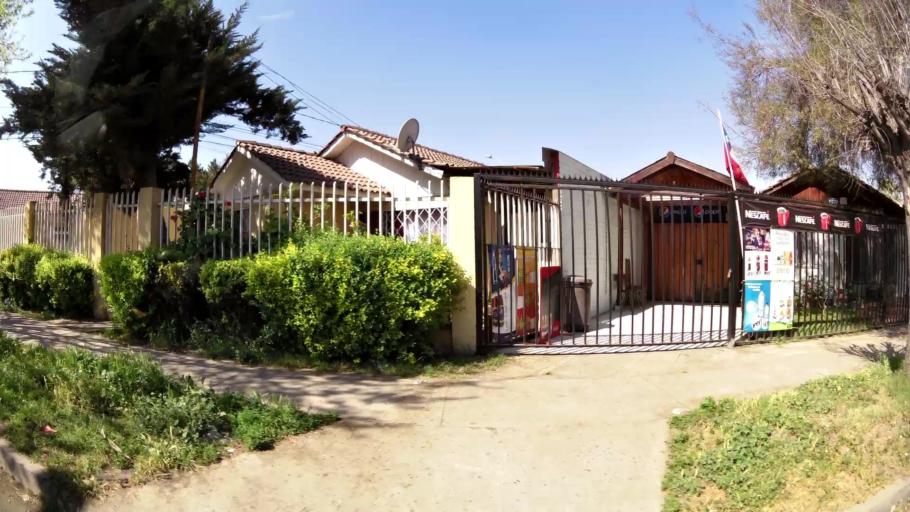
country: CL
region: Santiago Metropolitan
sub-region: Provincia de Santiago
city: Lo Prado
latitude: -33.3546
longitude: -70.7322
